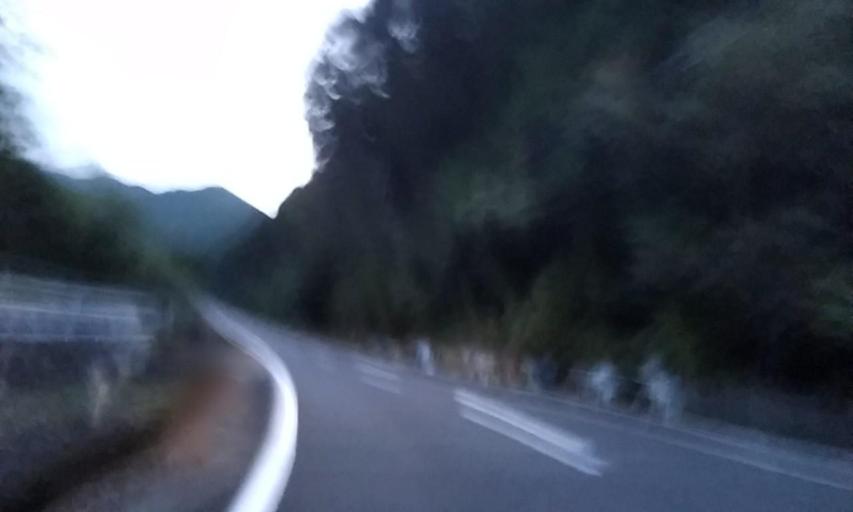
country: JP
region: Wakayama
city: Shingu
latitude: 33.7369
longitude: 135.9307
